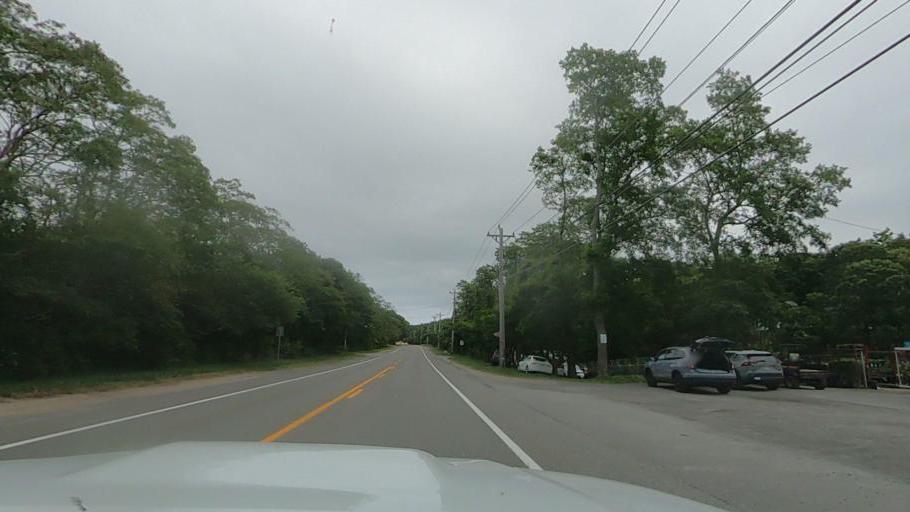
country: US
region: Massachusetts
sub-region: Barnstable County
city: Truro
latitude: 42.0062
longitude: -70.0612
